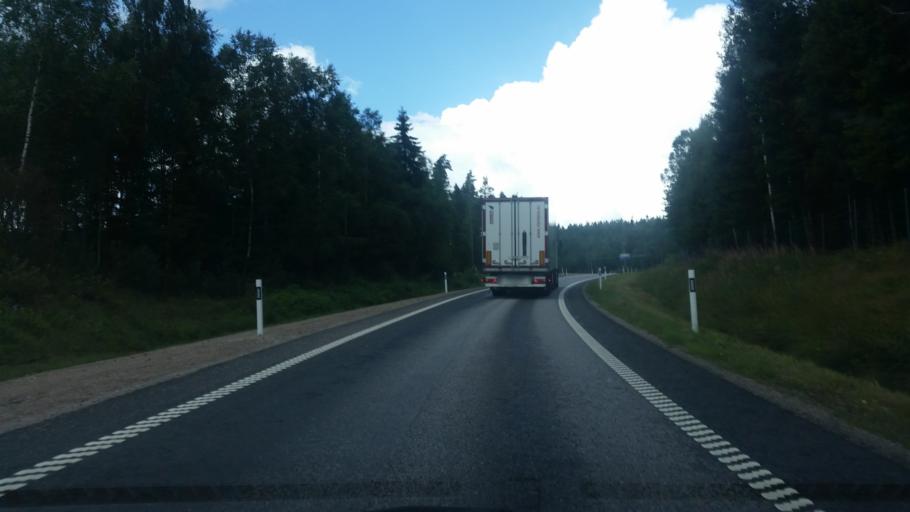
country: SE
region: Vaestra Goetaland
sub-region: Boras Kommun
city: Boras
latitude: 57.6812
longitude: 12.9410
